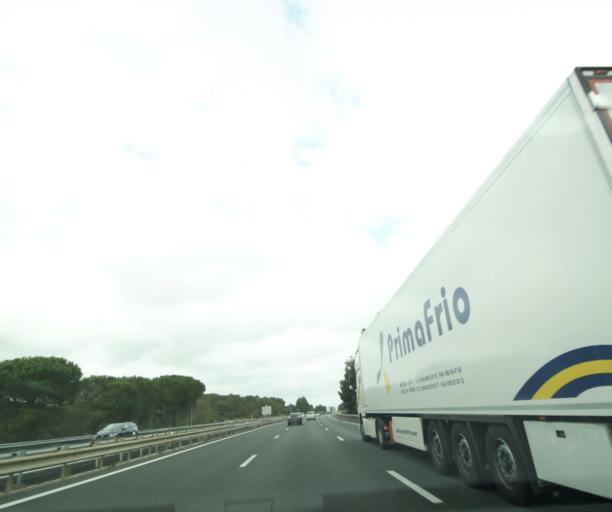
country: FR
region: Languedoc-Roussillon
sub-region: Departement de l'Herault
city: Montblanc
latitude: 43.3620
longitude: 3.3536
